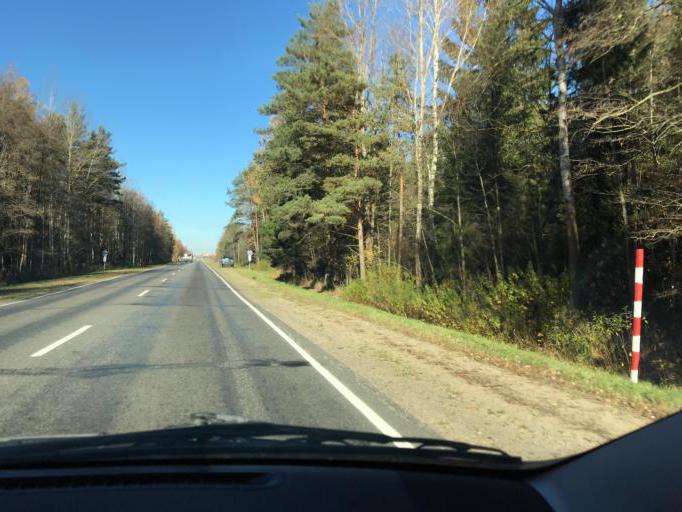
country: BY
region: Vitebsk
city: Polatsk
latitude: 55.4418
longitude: 28.7754
